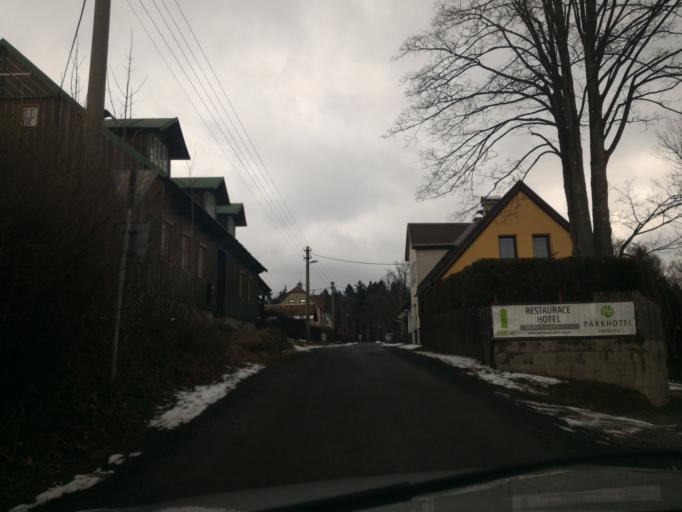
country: CZ
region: Liberecky
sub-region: Okres Jablonec nad Nisou
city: Smrzovka
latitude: 50.7326
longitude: 15.2418
